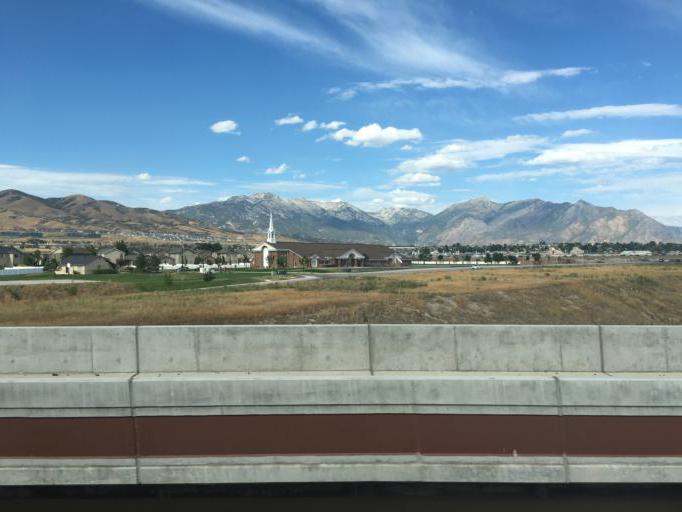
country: US
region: Utah
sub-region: Utah County
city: Lehi
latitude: 40.4124
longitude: -111.8819
